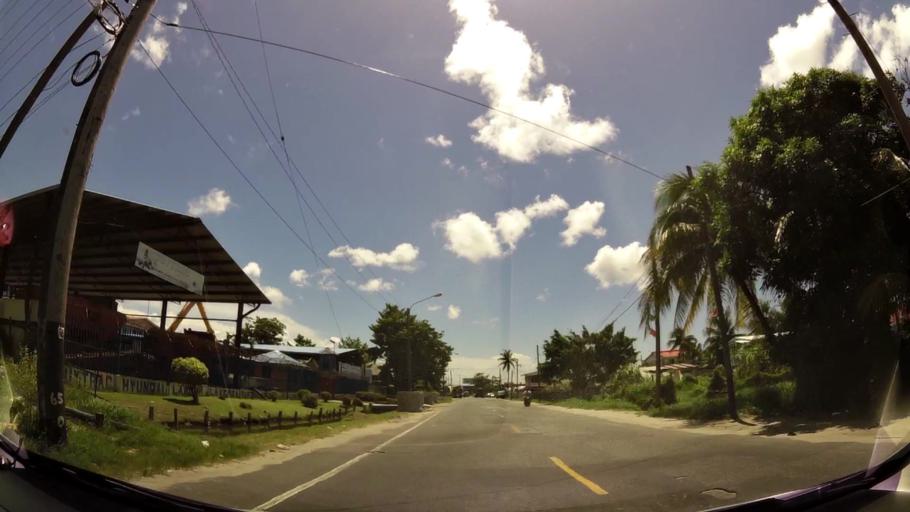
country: GY
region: Demerara-Mahaica
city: Georgetown
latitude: 6.7925
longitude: -58.1624
